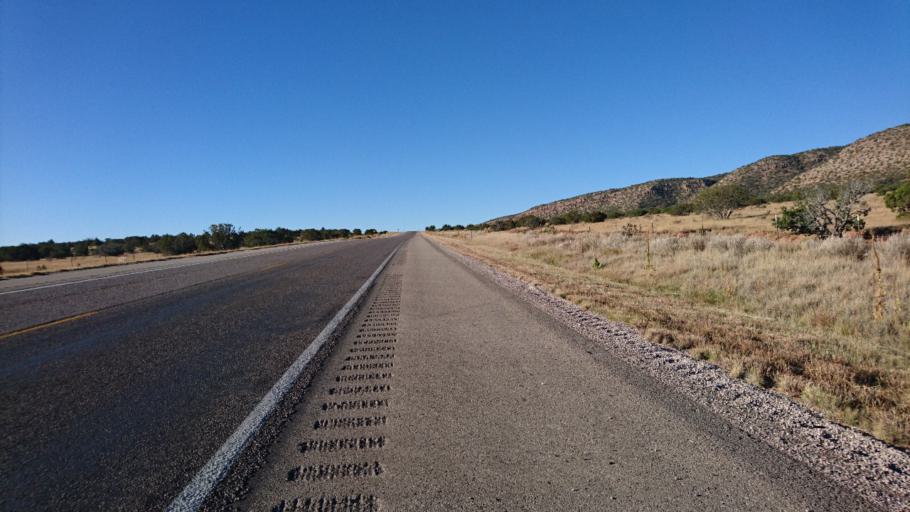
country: US
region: New Mexico
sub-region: Cibola County
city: Grants
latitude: 35.0050
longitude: -107.8927
